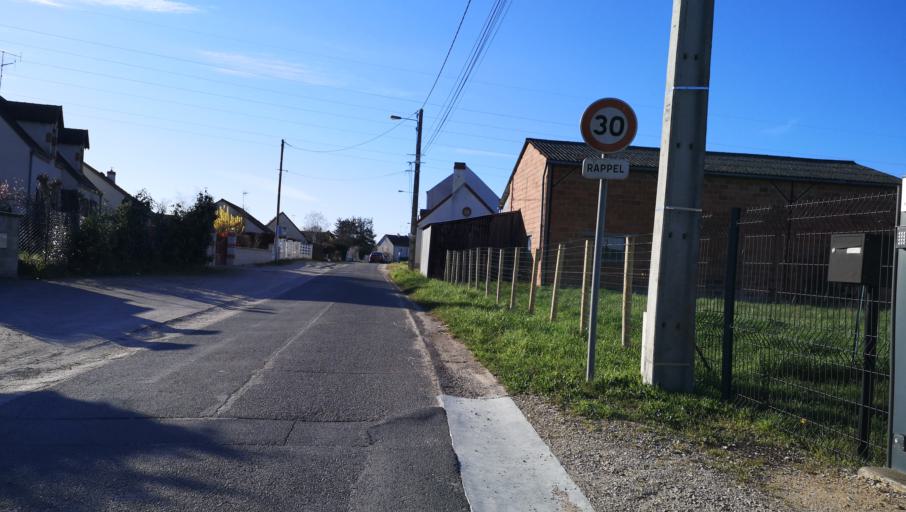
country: FR
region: Centre
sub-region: Departement du Loiret
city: Saint-Jean-de-Braye
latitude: 47.9215
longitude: 1.9742
